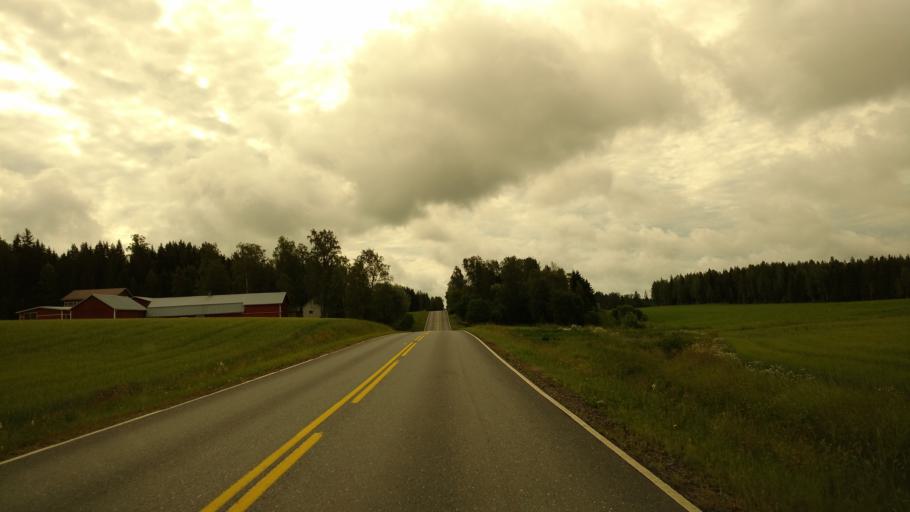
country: FI
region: Varsinais-Suomi
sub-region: Loimaa
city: Koski Tl
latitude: 60.5833
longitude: 23.1340
